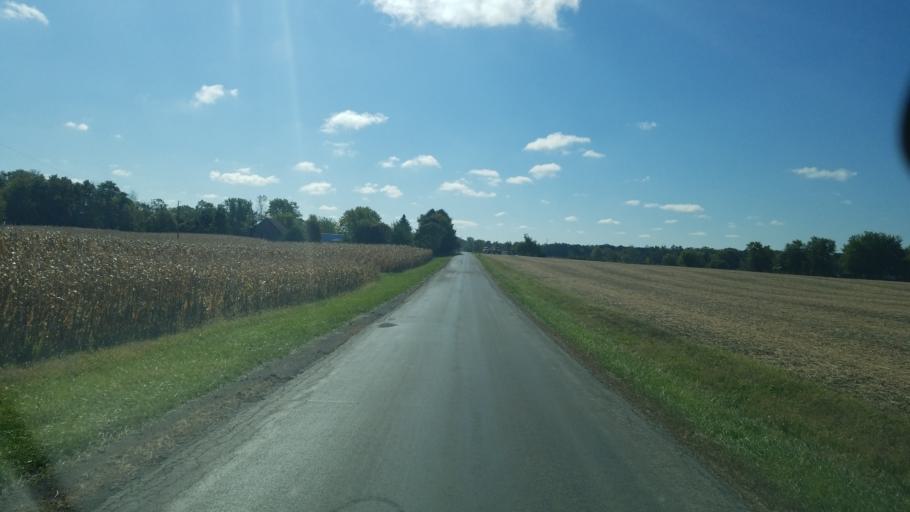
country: US
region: Ohio
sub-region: Highland County
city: Leesburg
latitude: 39.2734
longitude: -83.5535
